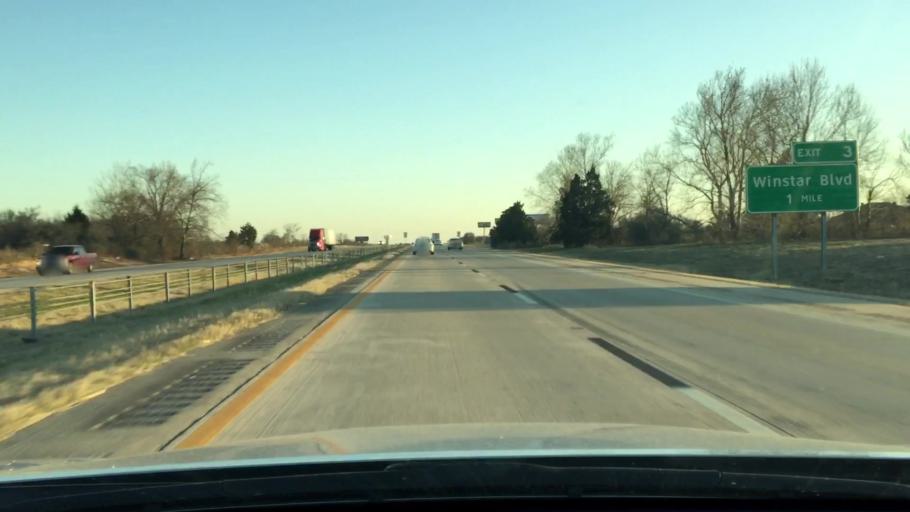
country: US
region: Oklahoma
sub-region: Love County
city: Marietta
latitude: 33.7887
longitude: -97.1350
